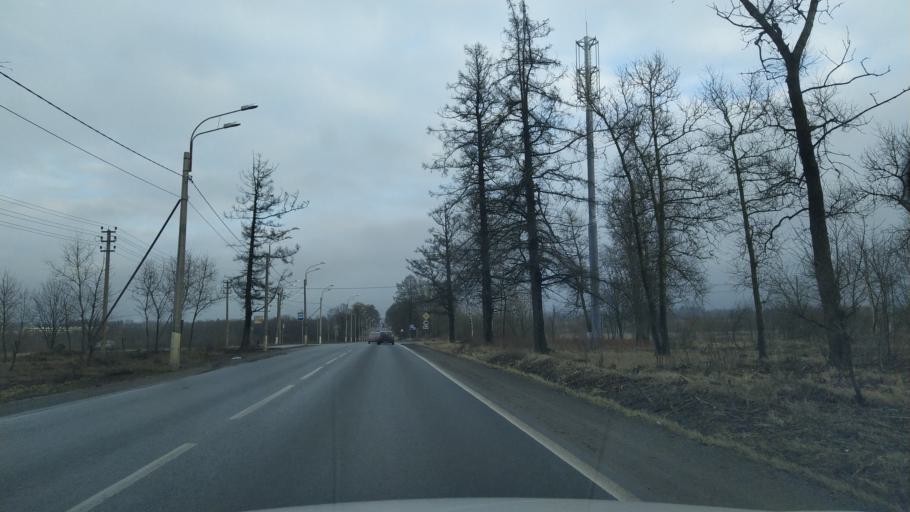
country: RU
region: St.-Petersburg
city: Aleksandrovskaya
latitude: 59.7095
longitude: 30.3226
